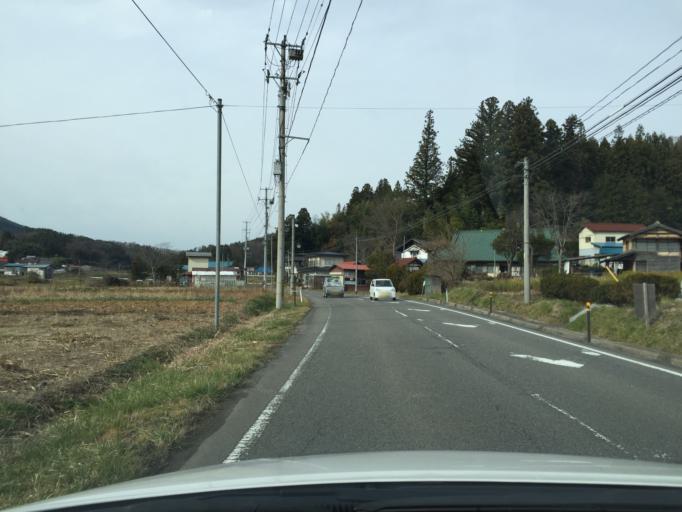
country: JP
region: Fukushima
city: Funehikimachi-funehiki
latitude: 37.3671
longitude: 140.6033
